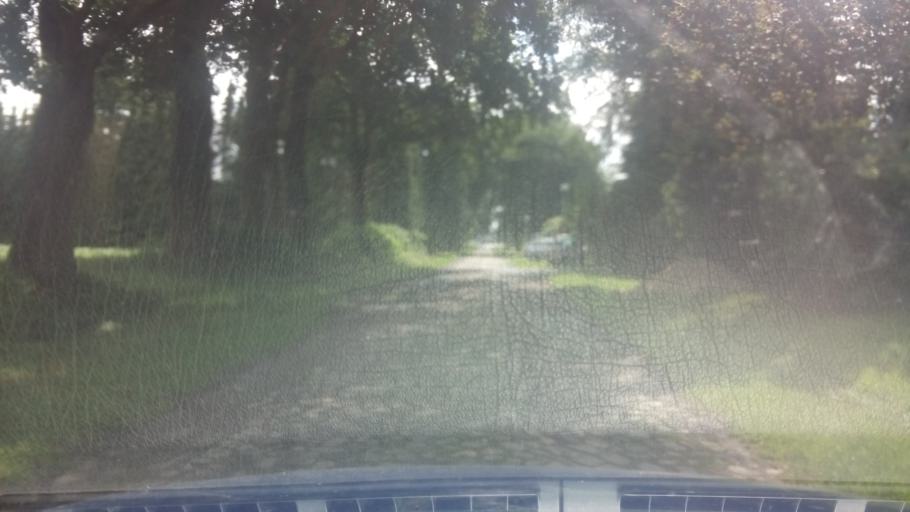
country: DE
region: Lower Saxony
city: Osterholz-Scharmbeck
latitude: 53.2349
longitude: 8.7500
